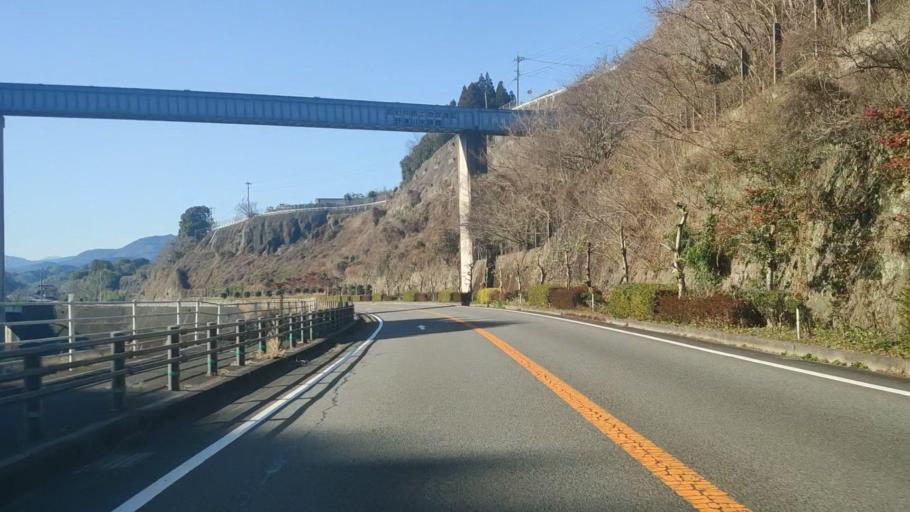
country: JP
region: Oita
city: Usuki
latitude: 33.0693
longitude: 131.6495
